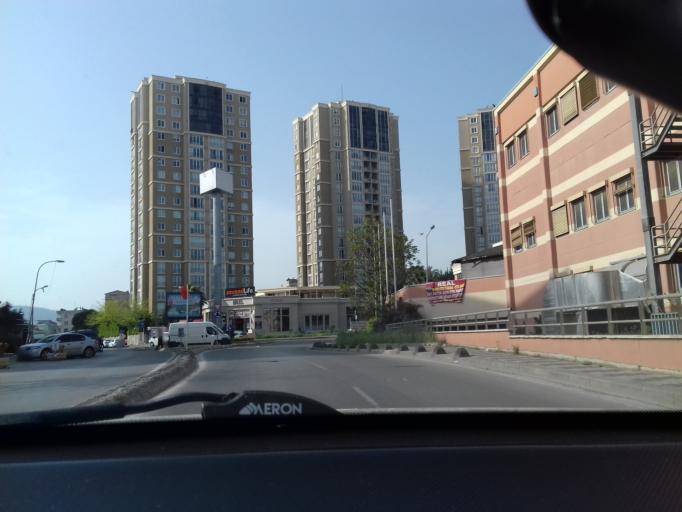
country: TR
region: Istanbul
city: Maltepe
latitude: 40.9125
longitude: 29.2104
